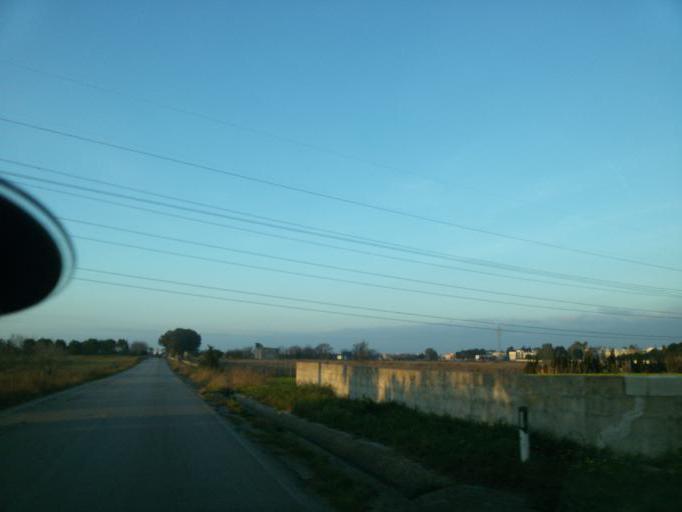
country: IT
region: Apulia
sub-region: Provincia di Brindisi
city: La Rosa
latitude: 40.6009
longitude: 17.9464
